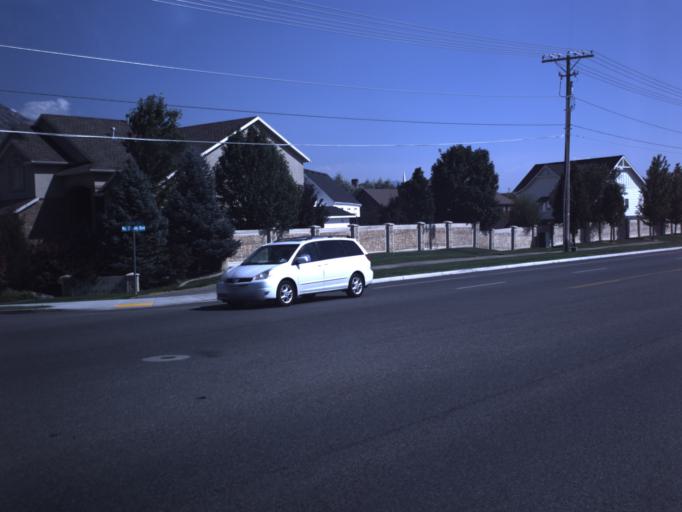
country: US
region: Utah
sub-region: Utah County
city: Cedar Hills
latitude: 40.4252
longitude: -111.7735
